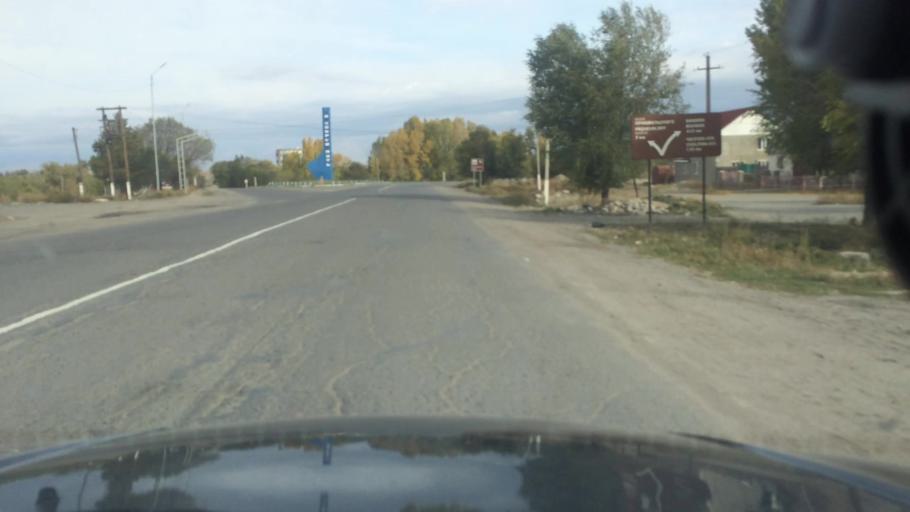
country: KG
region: Ysyk-Koel
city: Karakol
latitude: 42.5315
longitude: 78.3824
